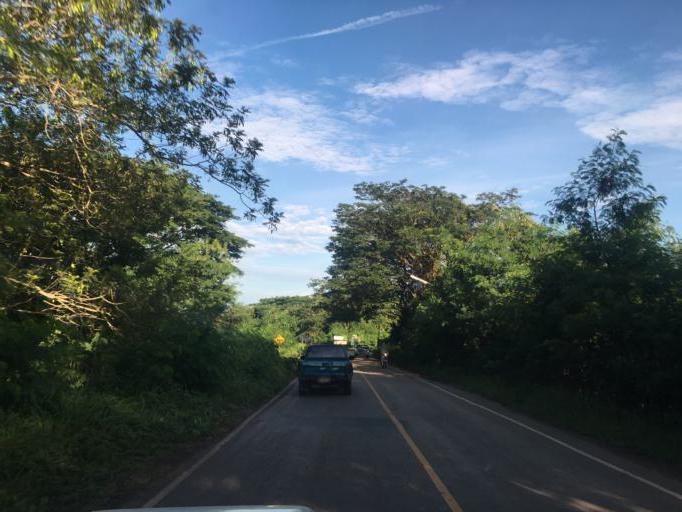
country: TH
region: Changwat Udon Thani
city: Kut Chap
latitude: 17.3802
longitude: 102.5976
